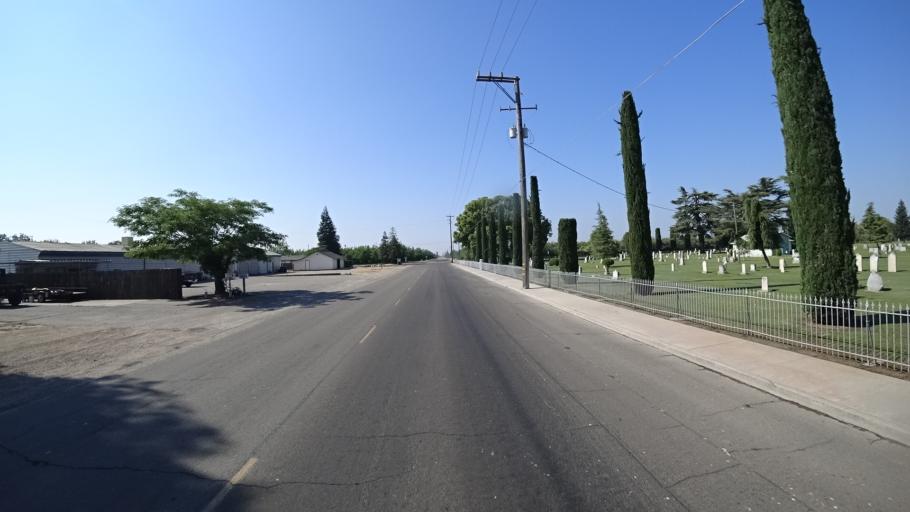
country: US
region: California
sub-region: Fresno County
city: Kingsburg
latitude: 36.5045
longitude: -119.5569
